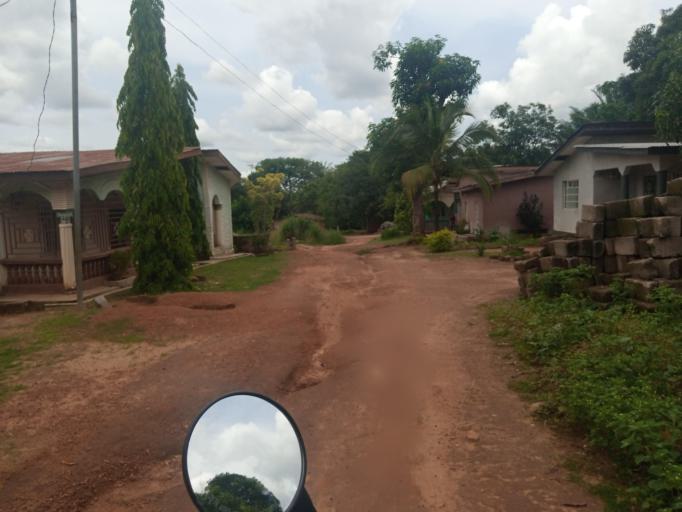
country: SL
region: Southern Province
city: Bo
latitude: 7.9577
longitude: -11.7155
